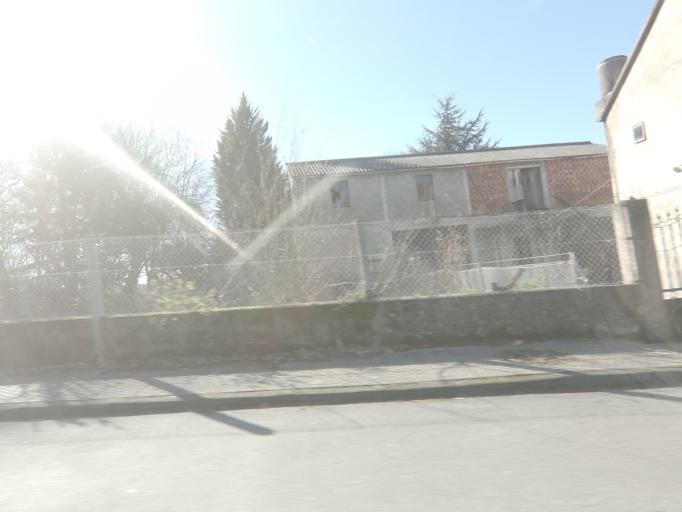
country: ES
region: Galicia
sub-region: Provincia de Pontevedra
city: Silleda
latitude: 42.6834
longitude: -8.1849
